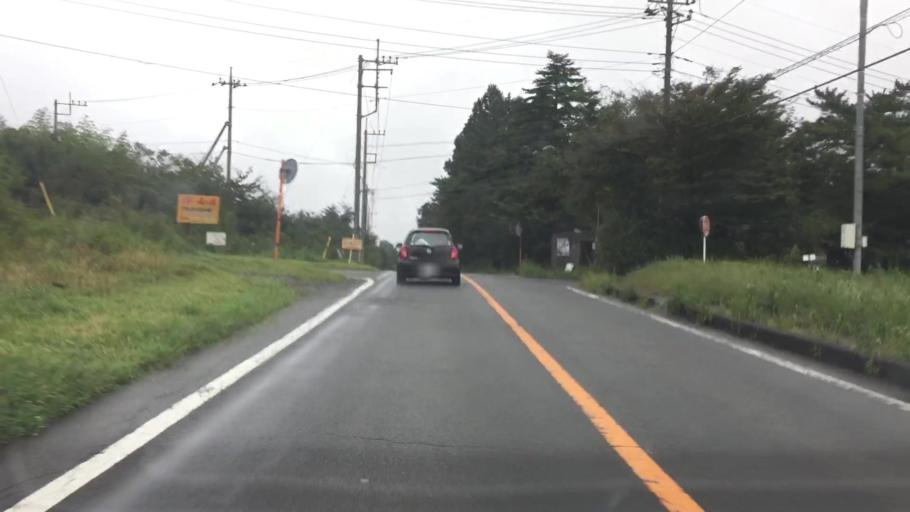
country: JP
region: Yamanashi
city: Fujikawaguchiko
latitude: 35.4068
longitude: 138.6155
